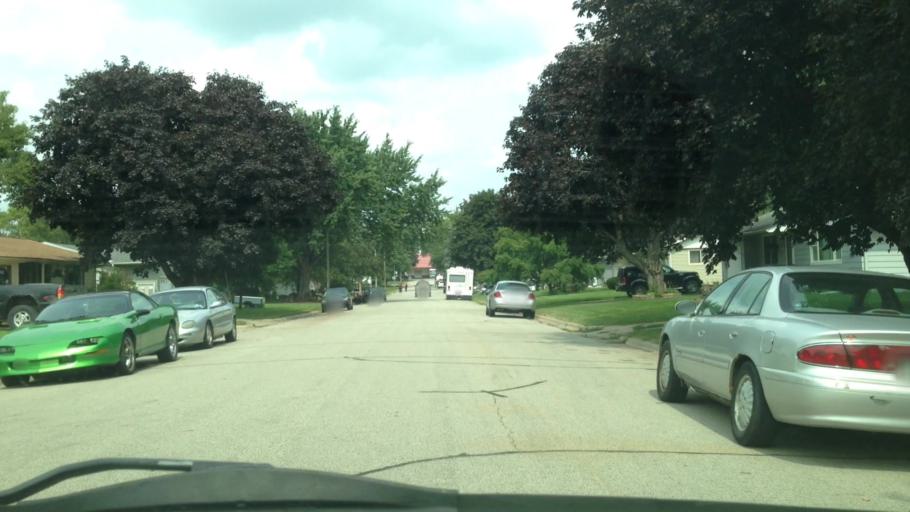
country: US
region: Minnesota
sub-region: Wabasha County
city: Plainview
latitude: 44.1611
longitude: -92.1740
